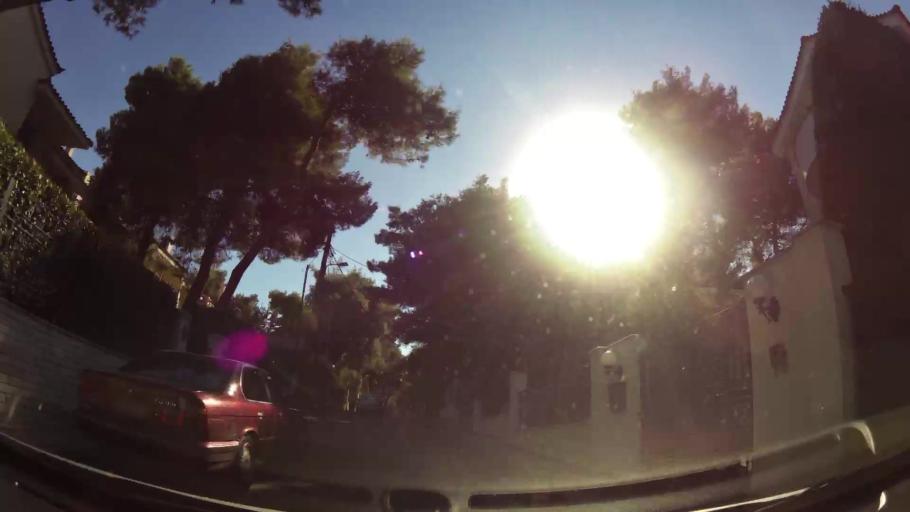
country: GR
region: Attica
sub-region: Nomarchia Athinas
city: Ekali
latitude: 38.1184
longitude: 23.8421
